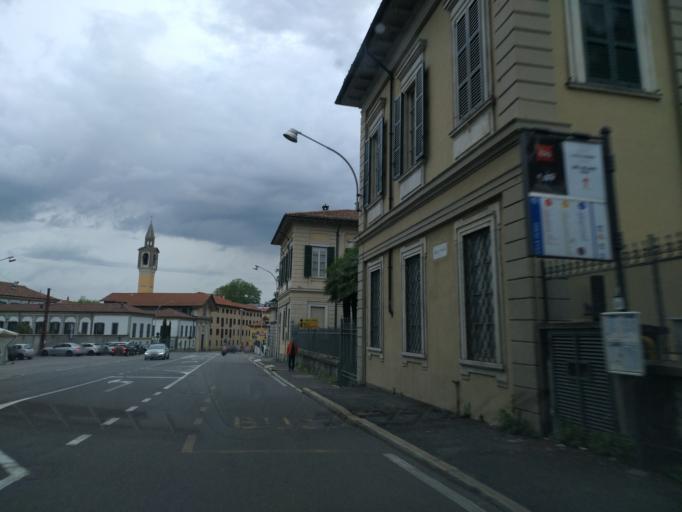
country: IT
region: Lombardy
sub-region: Provincia di Como
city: San Fermo della Battaglia
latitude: 45.8175
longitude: 9.0645
